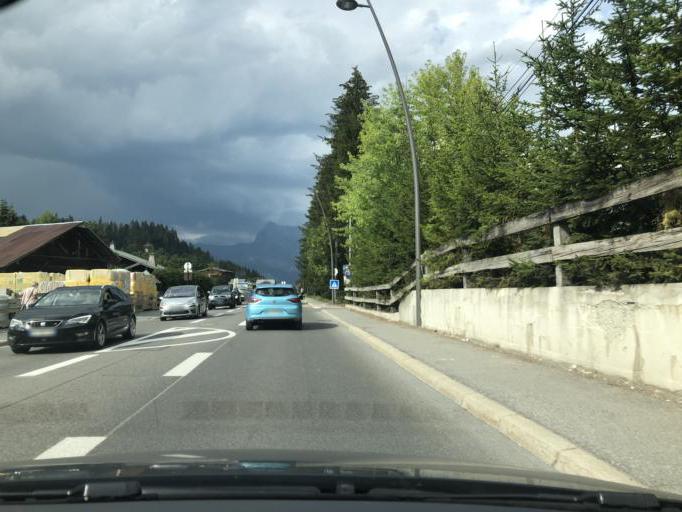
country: FR
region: Rhone-Alpes
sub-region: Departement de la Haute-Savoie
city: Megeve
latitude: 45.8659
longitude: 6.6265
